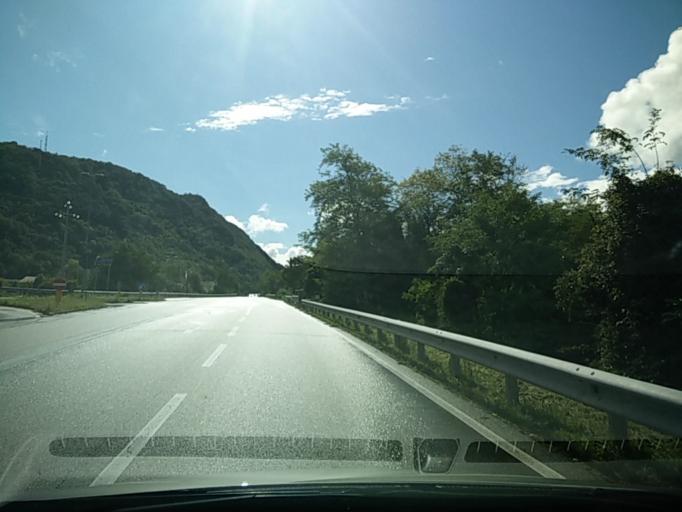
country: IT
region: Veneto
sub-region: Provincia di Treviso
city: Segusino
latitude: 45.9129
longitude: 11.9501
